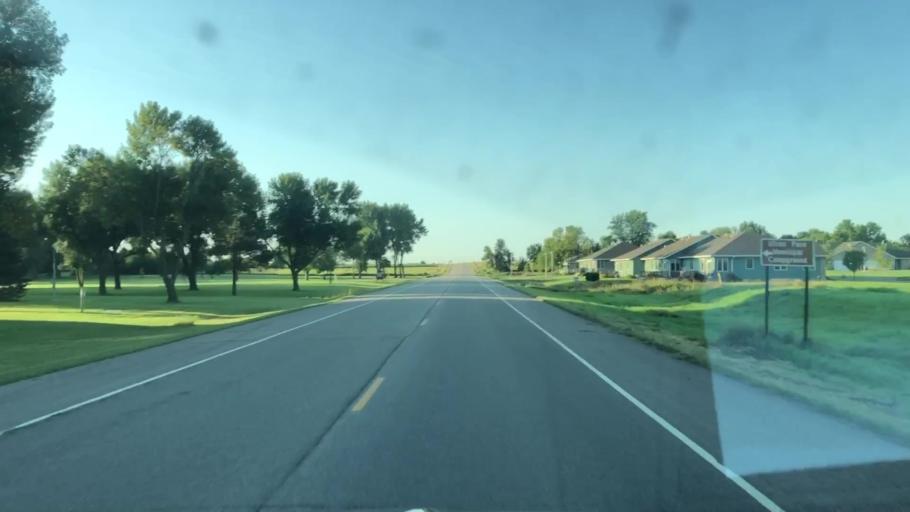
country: US
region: Minnesota
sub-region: Nobles County
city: Worthington
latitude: 43.6081
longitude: -95.6366
